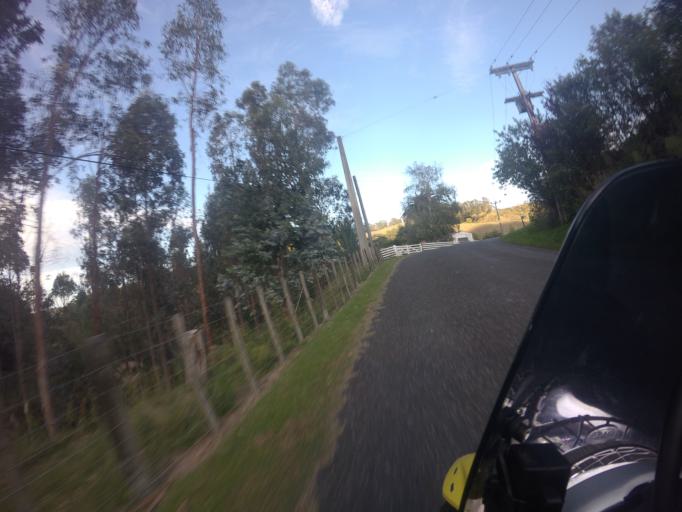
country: NZ
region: Gisborne
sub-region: Gisborne District
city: Gisborne
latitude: -38.6567
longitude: 178.0528
